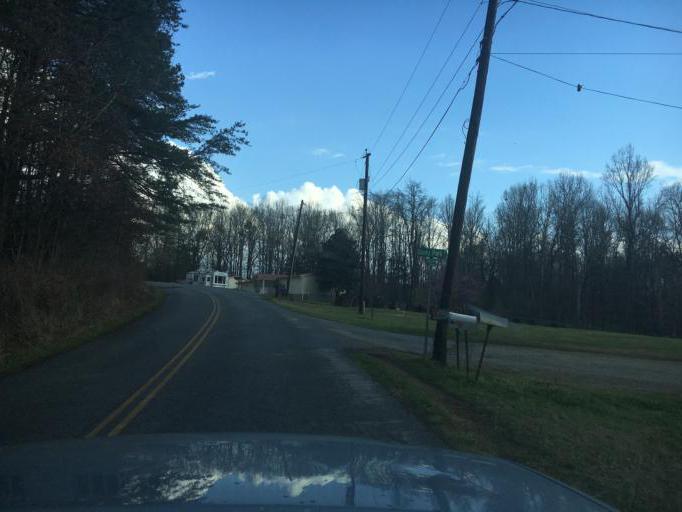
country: US
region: South Carolina
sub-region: Greenville County
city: Berea
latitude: 34.8673
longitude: -82.5175
